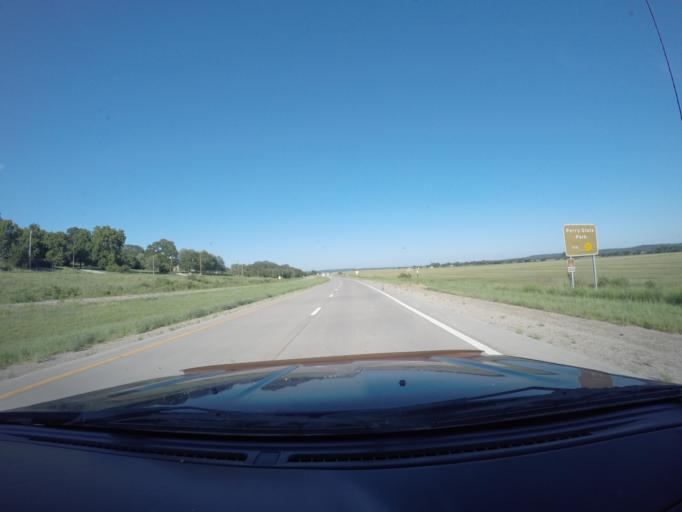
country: US
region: Kansas
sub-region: Shawnee County
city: Topeka
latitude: 39.0864
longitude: -95.4821
